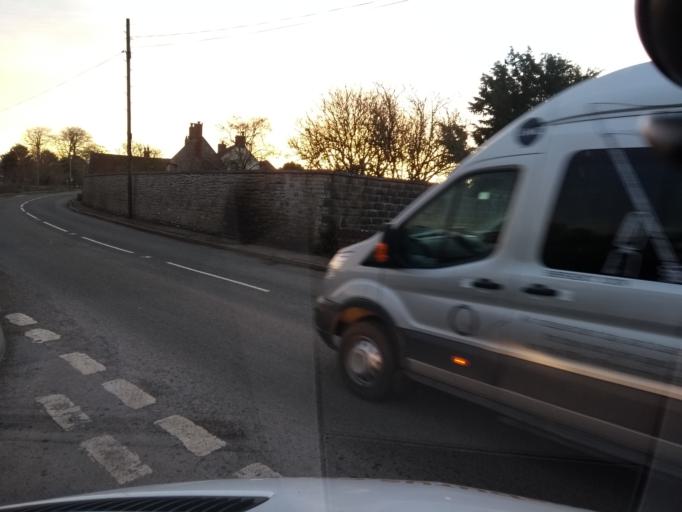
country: GB
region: England
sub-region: Somerset
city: Wedmore
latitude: 51.2250
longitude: -2.8582
